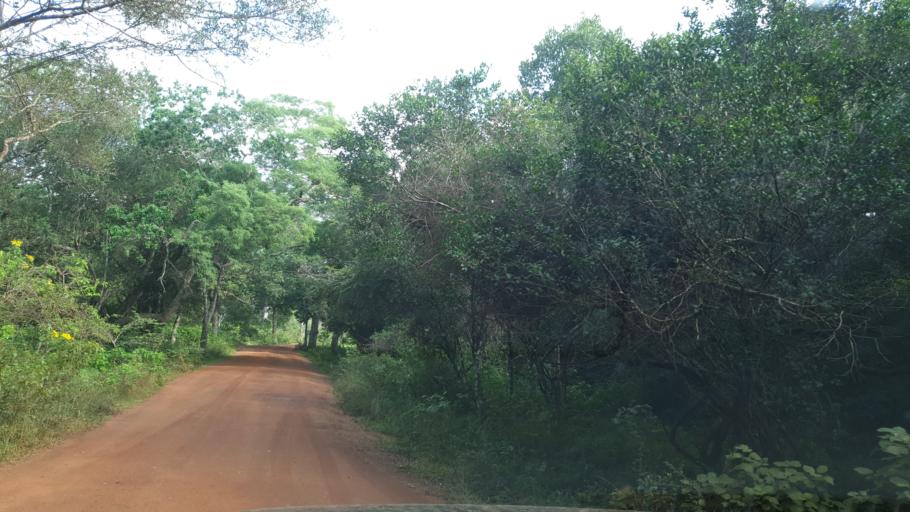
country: LK
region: North Central
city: Anuradhapura
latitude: 8.3787
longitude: 80.0687
